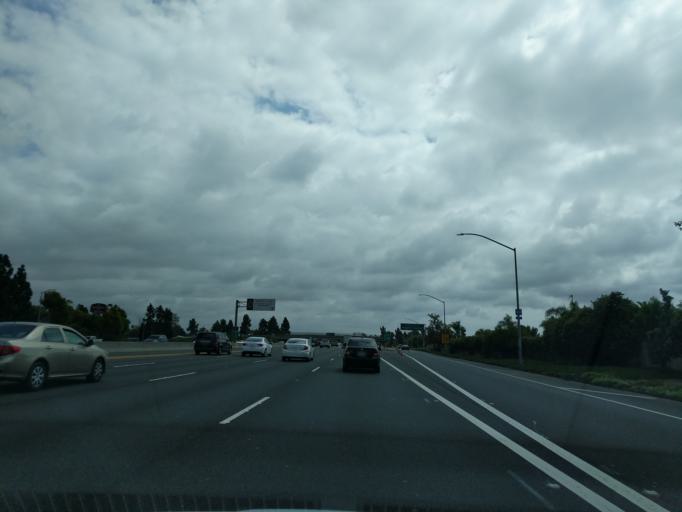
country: US
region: California
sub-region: Orange County
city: Fountain Valley
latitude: 33.7083
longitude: -117.9582
